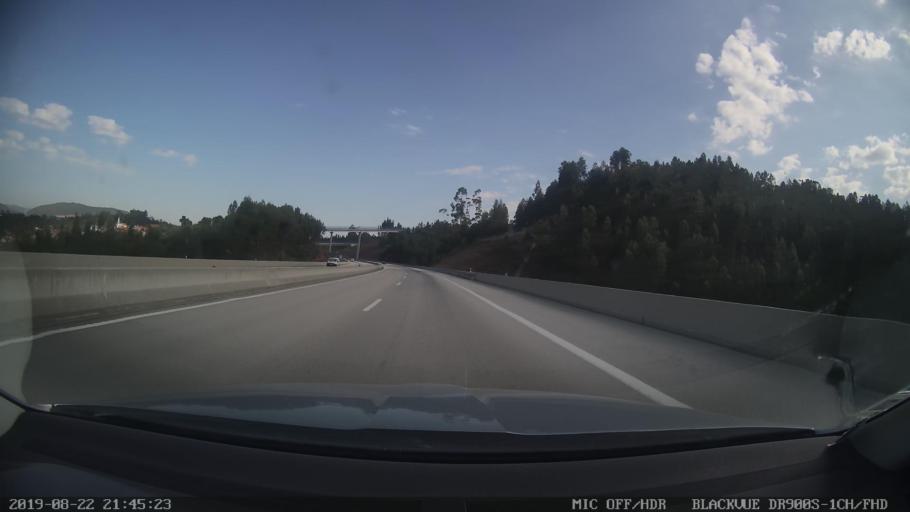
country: PT
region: Coimbra
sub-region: Penela
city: Penela
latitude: 39.9688
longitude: -8.3522
